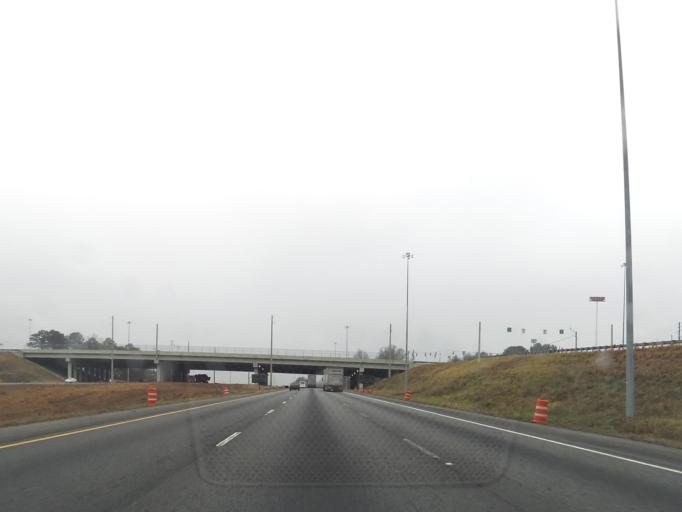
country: US
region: Georgia
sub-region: Henry County
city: Stockbridge
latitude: 33.5044
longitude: -84.2290
